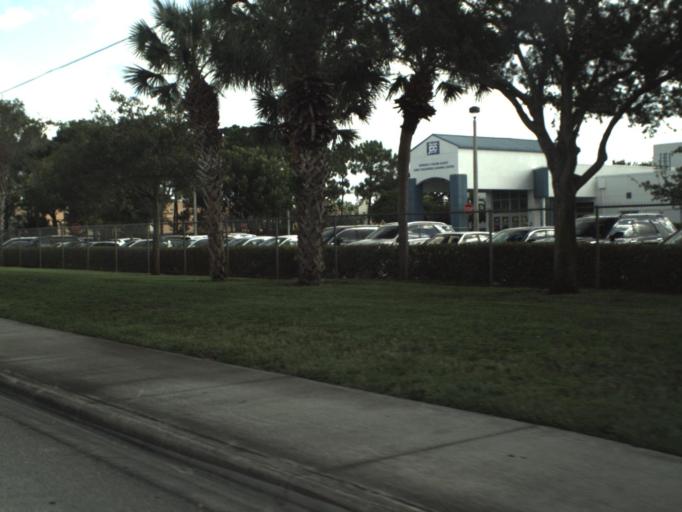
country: US
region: Florida
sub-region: Palm Beach County
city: Seminole Manor
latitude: 26.5491
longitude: -80.1493
